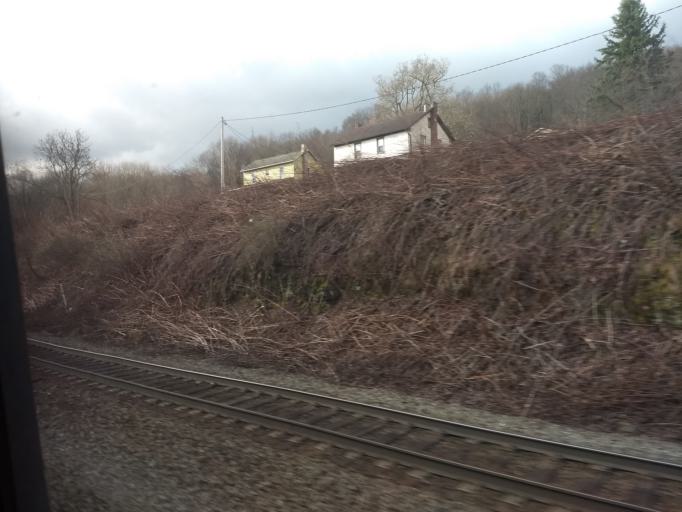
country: US
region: Pennsylvania
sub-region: Cambria County
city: Vinco
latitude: 40.3764
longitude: -78.8340
